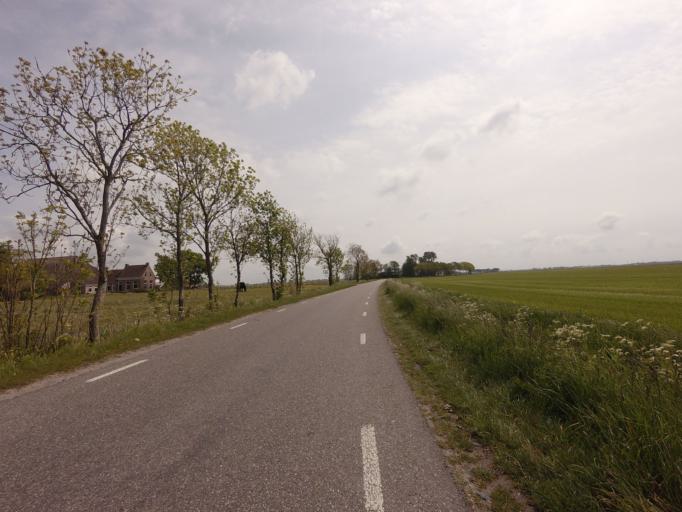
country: NL
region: Friesland
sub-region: Sudwest Fryslan
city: Bolsward
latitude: 53.1117
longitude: 5.4894
